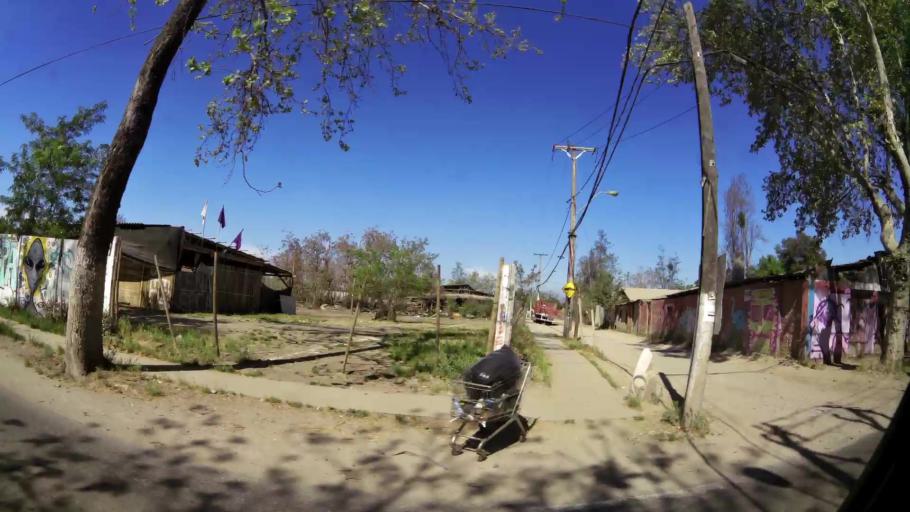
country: CL
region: Santiago Metropolitan
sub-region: Provincia de Talagante
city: Penaflor
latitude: -33.6018
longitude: -70.8947
